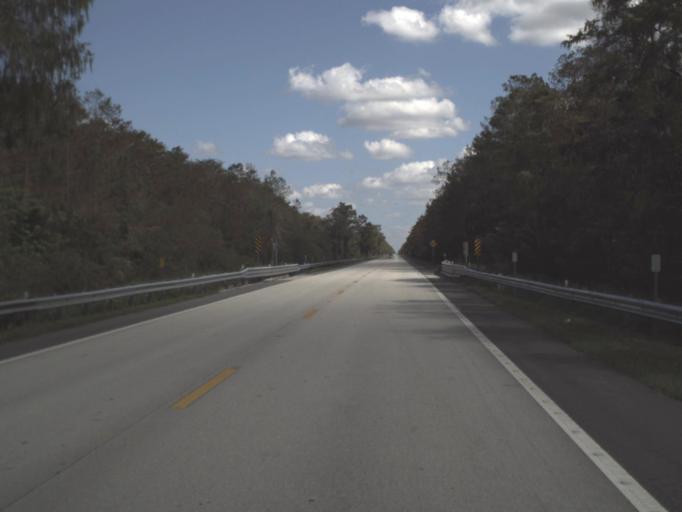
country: US
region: Florida
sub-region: Miami-Dade County
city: Kendall West
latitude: 25.8543
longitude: -81.0079
